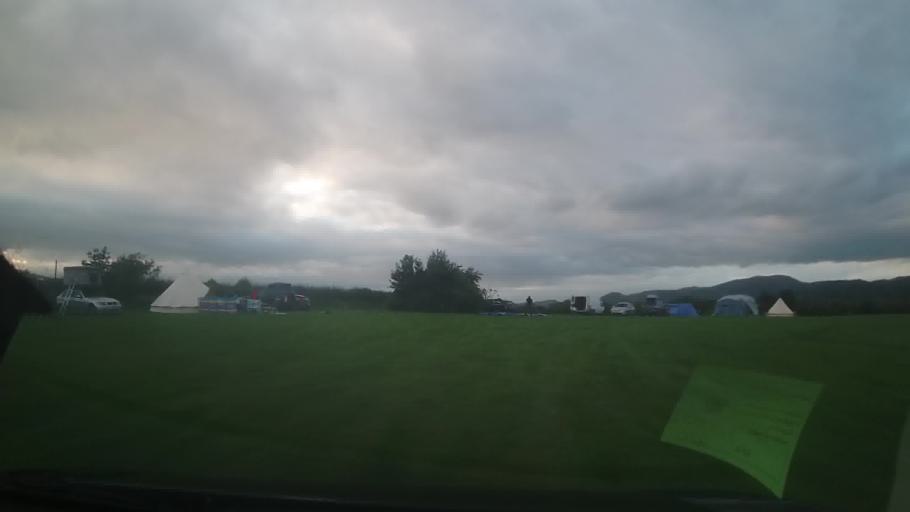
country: GB
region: England
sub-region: Shropshire
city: Bishop's Castle
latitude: 52.5012
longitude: -2.9987
